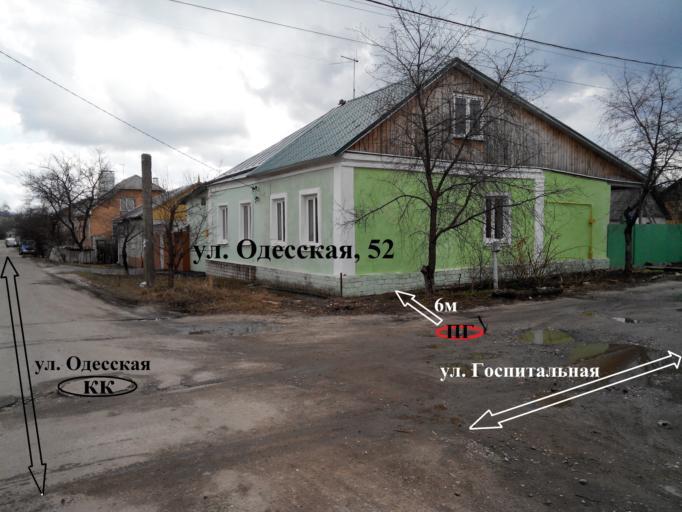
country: RU
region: Voronezj
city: Voronezh
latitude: 51.6343
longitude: 39.1658
